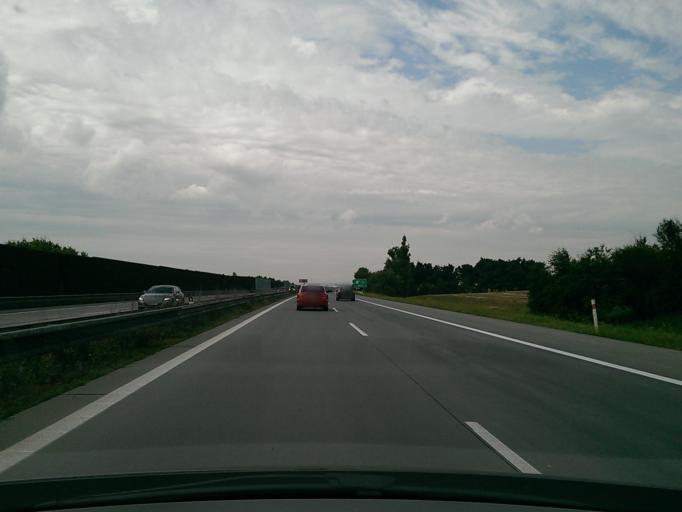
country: CZ
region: Vysocina
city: Merin
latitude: 49.3921
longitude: 15.8997
